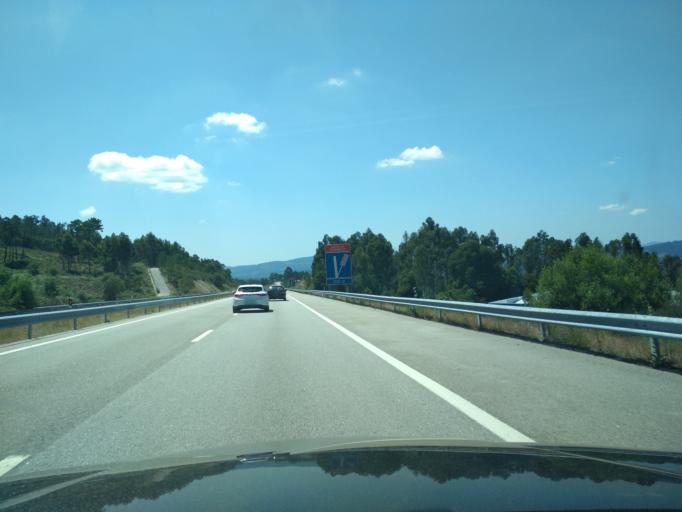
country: PT
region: Braga
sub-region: Fafe
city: Fafe
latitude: 41.4414
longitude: -8.1142
